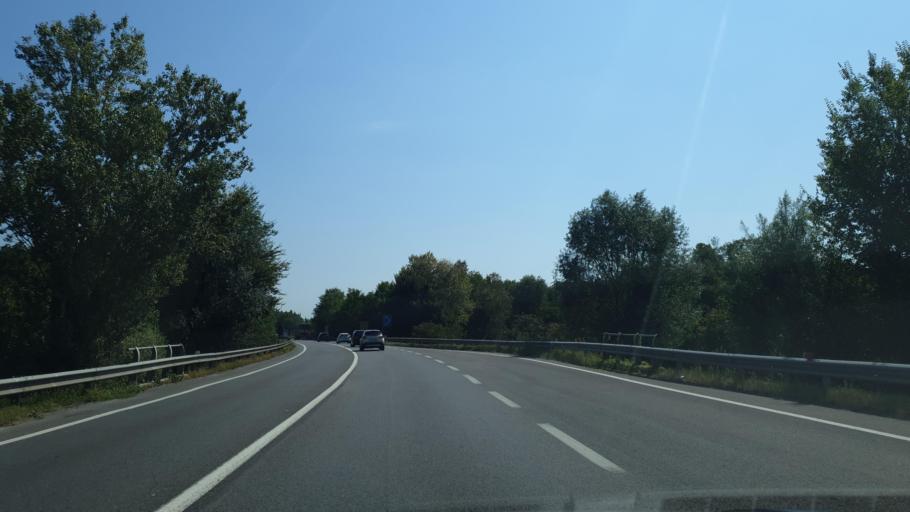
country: IT
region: Lombardy
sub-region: Provincia di Brescia
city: Lonato
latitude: 45.4685
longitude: 10.4950
